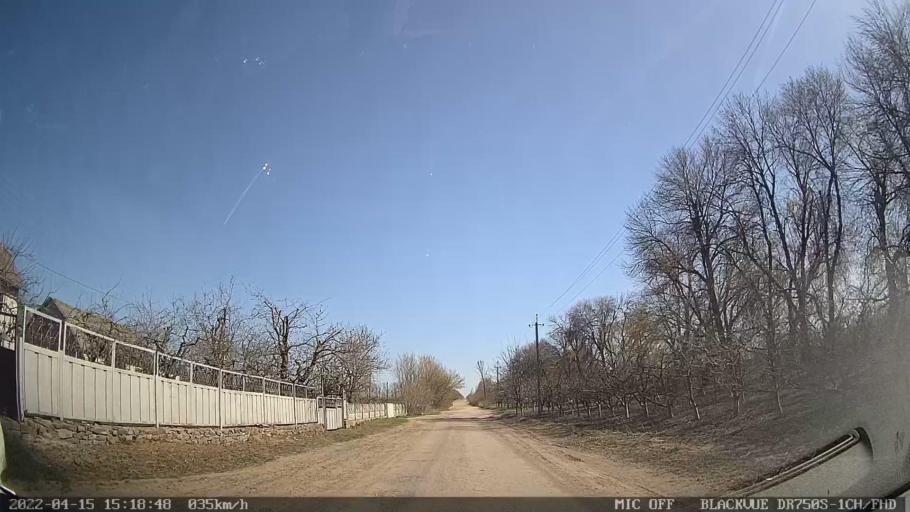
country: MD
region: Raionul Ocnita
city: Otaci
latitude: 48.3892
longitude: 27.9040
